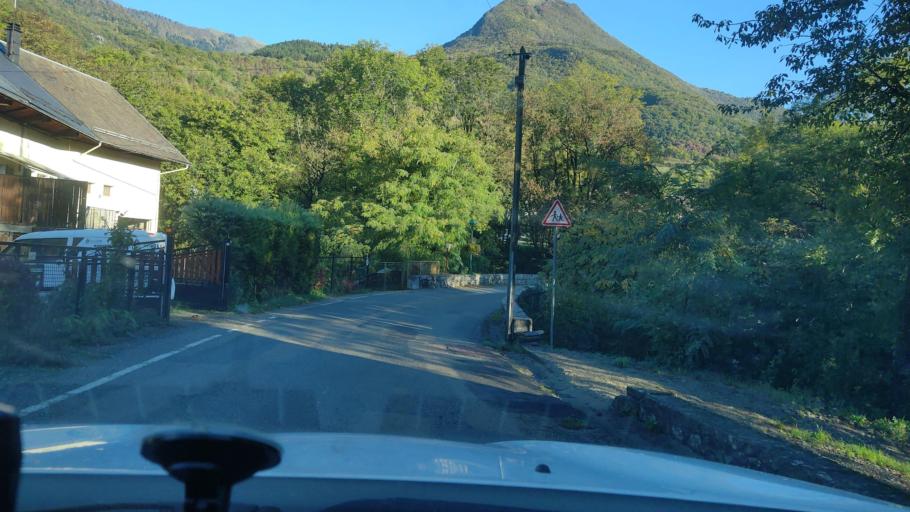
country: FR
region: Rhone-Alpes
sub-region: Departement de la Savoie
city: Cruet
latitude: 45.5281
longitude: 6.0921
